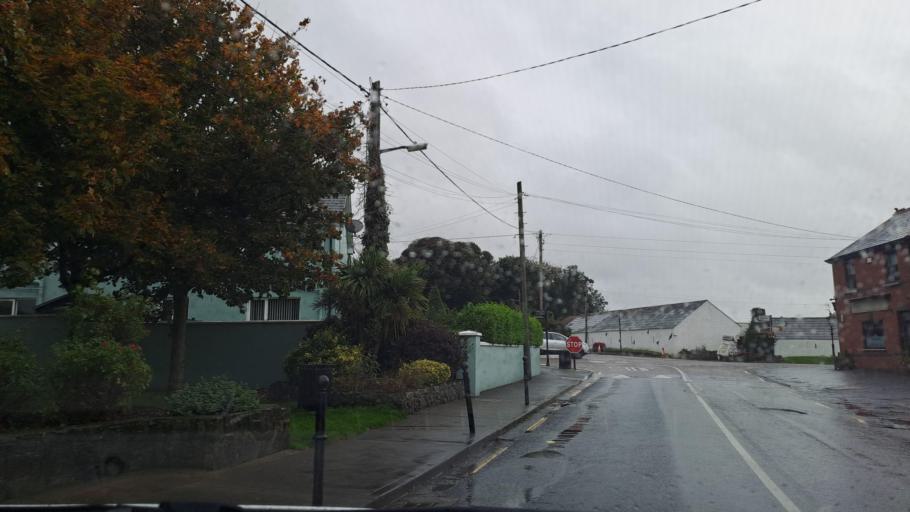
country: IE
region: Leinster
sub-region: Lu
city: Dundalk
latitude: 53.9720
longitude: -6.4873
